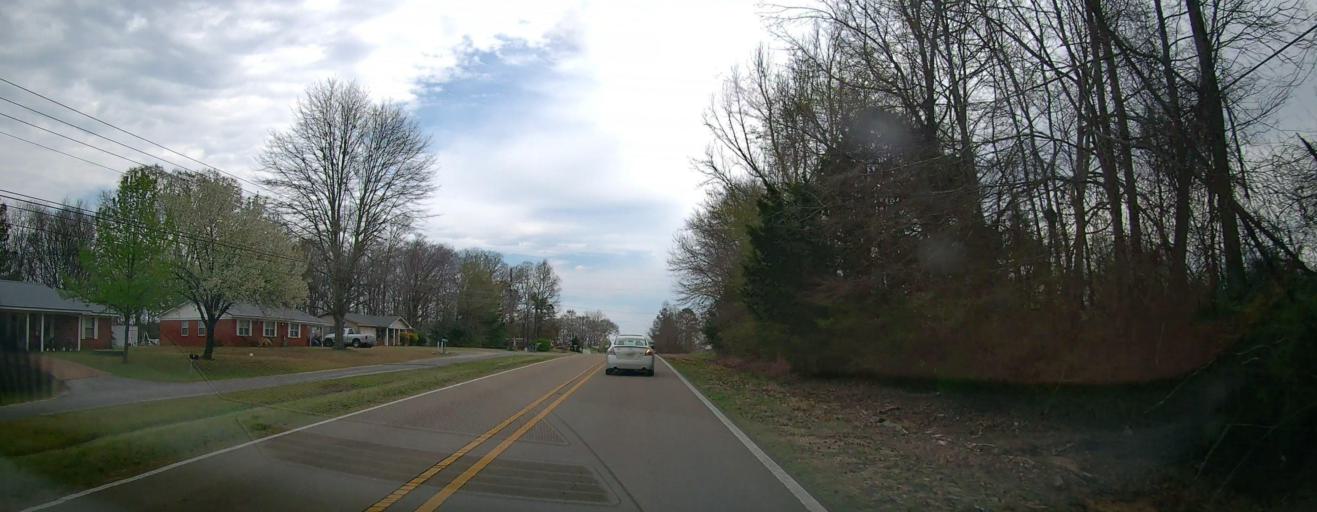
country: US
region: Mississippi
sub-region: Itawamba County
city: Fulton
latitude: 34.2708
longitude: -88.3386
